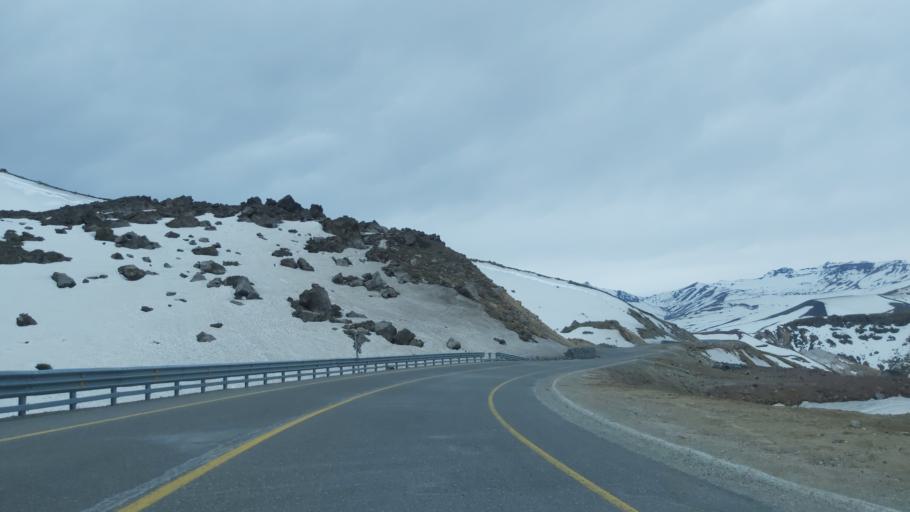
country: CL
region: Maule
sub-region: Provincia de Linares
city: Colbun
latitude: -35.9976
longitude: -70.5605
